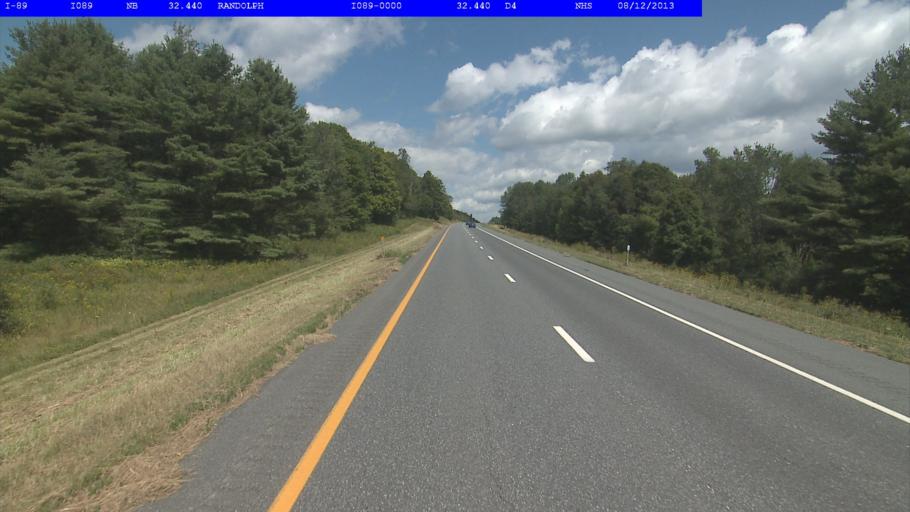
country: US
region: Vermont
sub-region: Orange County
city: Randolph
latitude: 43.9665
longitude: -72.6247
